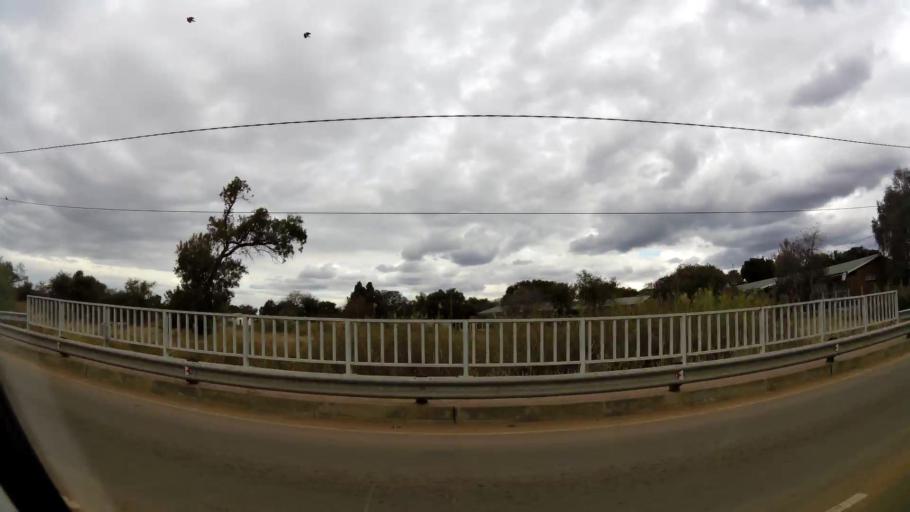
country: ZA
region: Limpopo
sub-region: Waterberg District Municipality
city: Modimolle
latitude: -24.7025
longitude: 28.4131
